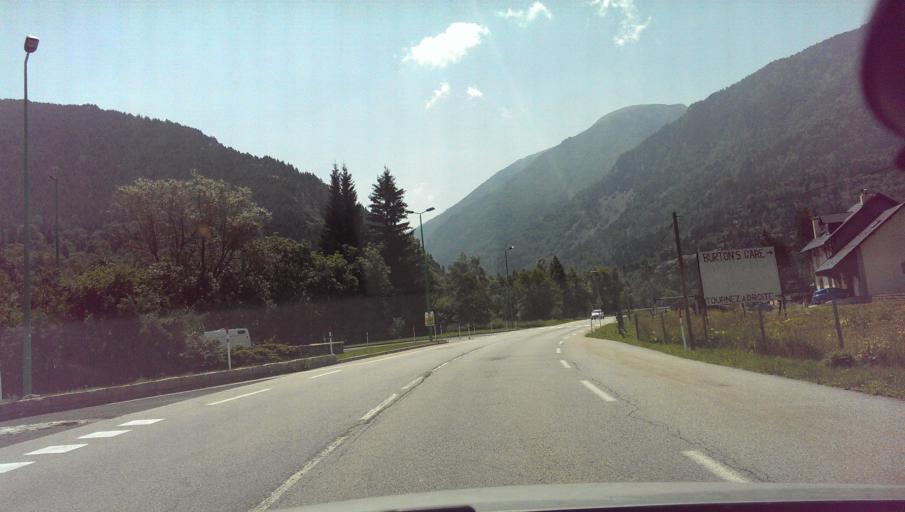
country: ES
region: Catalonia
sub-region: Provincia de Girona
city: Meranges
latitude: 42.5231
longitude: 1.8228
